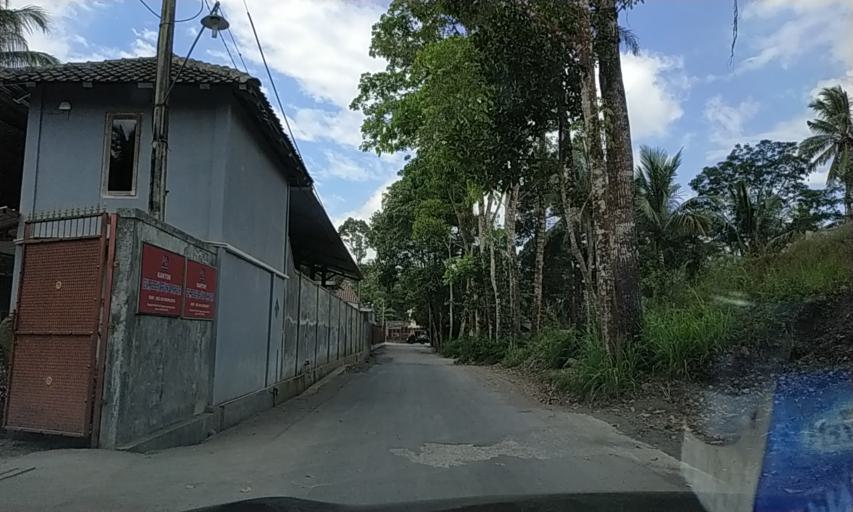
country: ID
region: Central Java
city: Jogonalan
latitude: -7.6284
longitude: 110.4753
